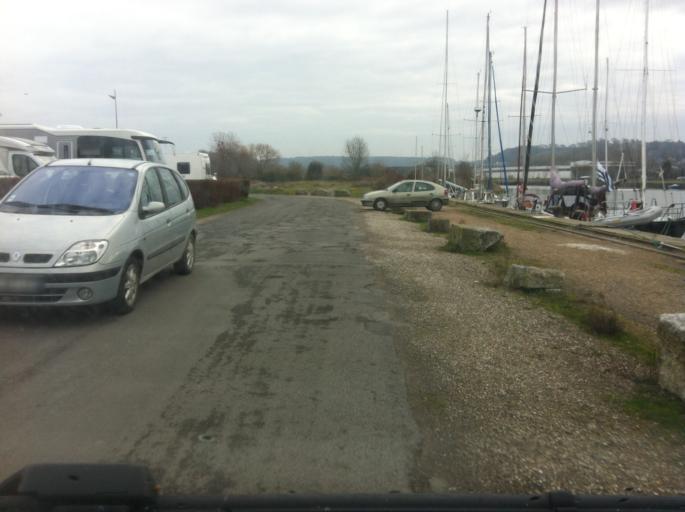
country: FR
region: Lower Normandy
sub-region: Departement du Calvados
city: Honfleur
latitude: 49.4191
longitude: 0.2427
